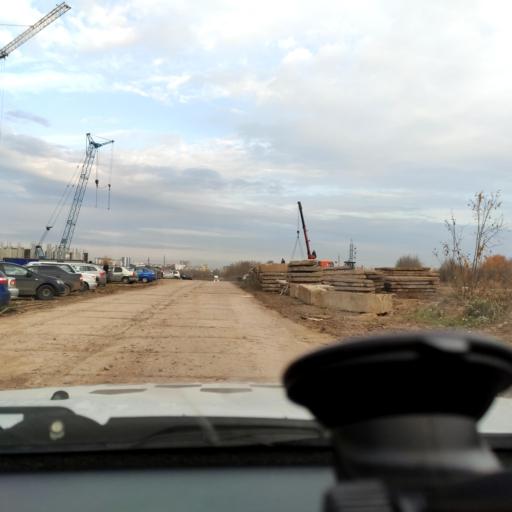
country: RU
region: Perm
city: Perm
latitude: 58.0113
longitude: 56.3328
